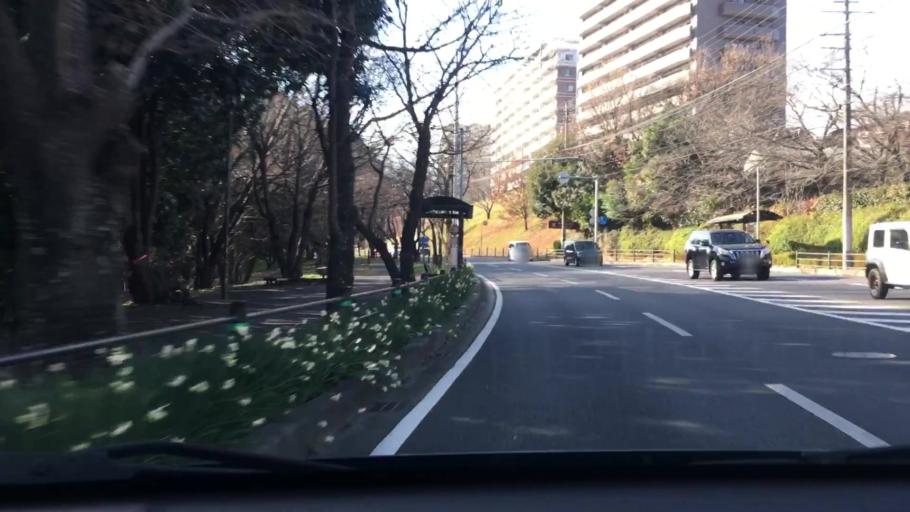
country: JP
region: Oita
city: Tsurusaki
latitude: 33.2256
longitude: 131.6558
